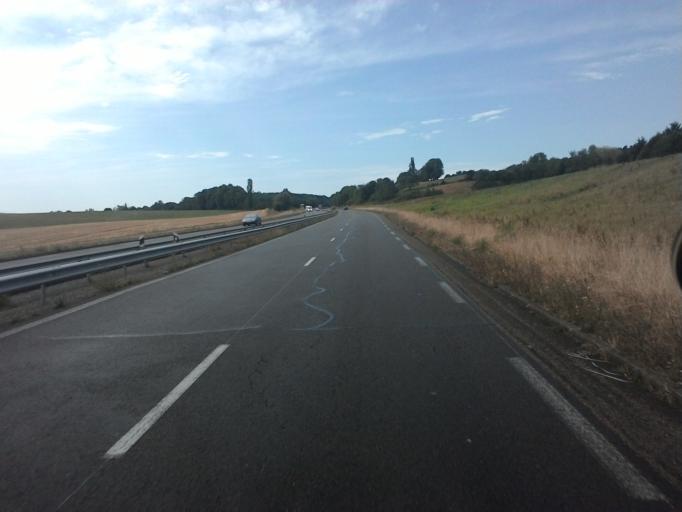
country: FR
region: Franche-Comte
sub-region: Departement du Jura
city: Lons-le-Saunier
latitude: 46.7269
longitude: 5.5577
